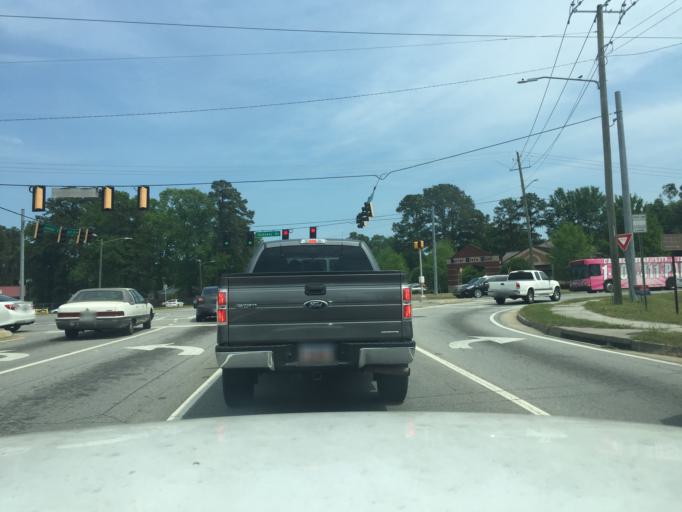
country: US
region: Georgia
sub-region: Chatham County
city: Isle of Hope
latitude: 32.0003
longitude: -81.0779
